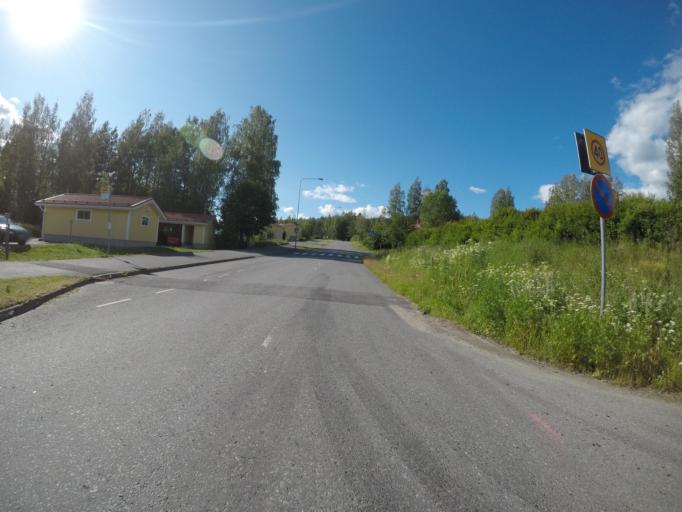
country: FI
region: Haeme
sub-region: Haemeenlinna
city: Haemeenlinna
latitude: 61.0210
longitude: 24.5197
